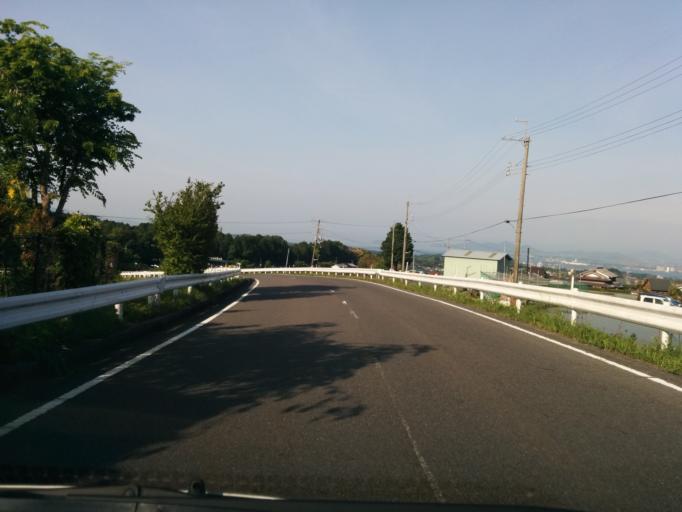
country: JP
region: Shiga Prefecture
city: Kitahama
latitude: 35.1049
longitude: 135.8681
